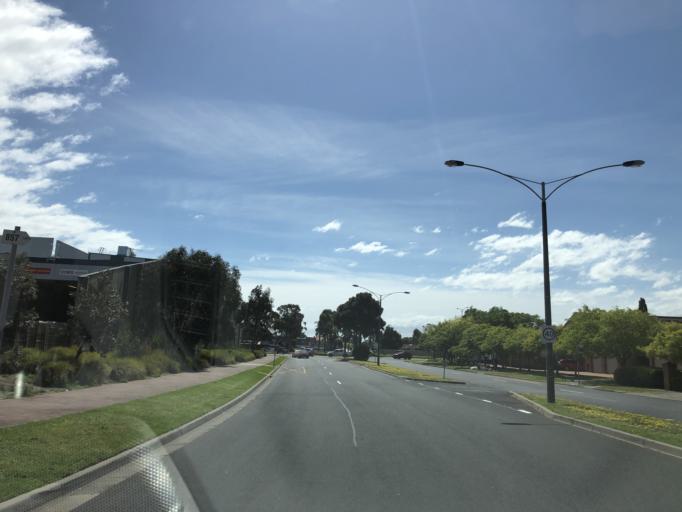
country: AU
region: Victoria
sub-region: Kingston
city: Patterson Lakes
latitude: -38.0692
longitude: 145.1454
